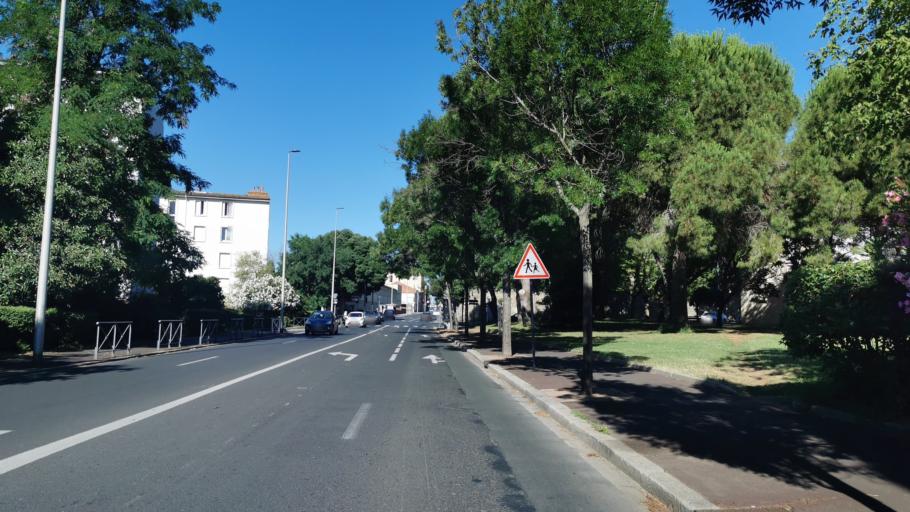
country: FR
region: Languedoc-Roussillon
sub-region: Departement de l'Herault
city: Beziers
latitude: 43.3451
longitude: 3.2354
